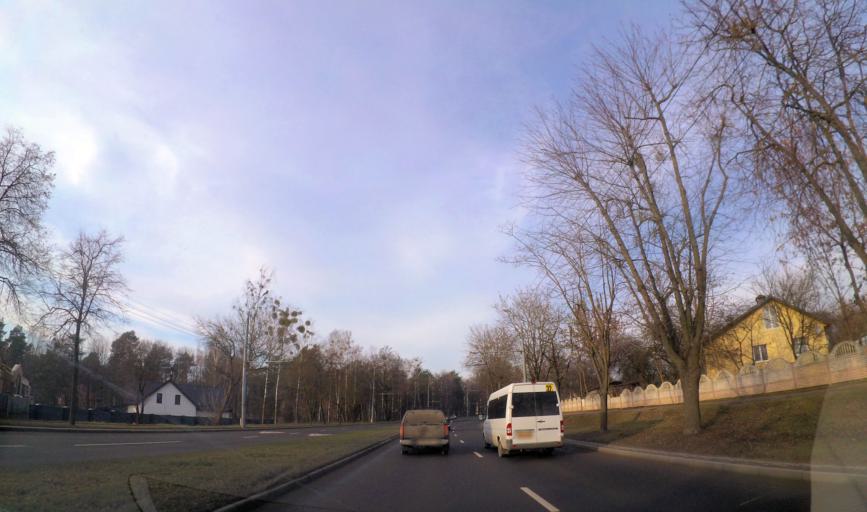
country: BY
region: Grodnenskaya
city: Hrodna
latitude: 53.6849
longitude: 23.8025
